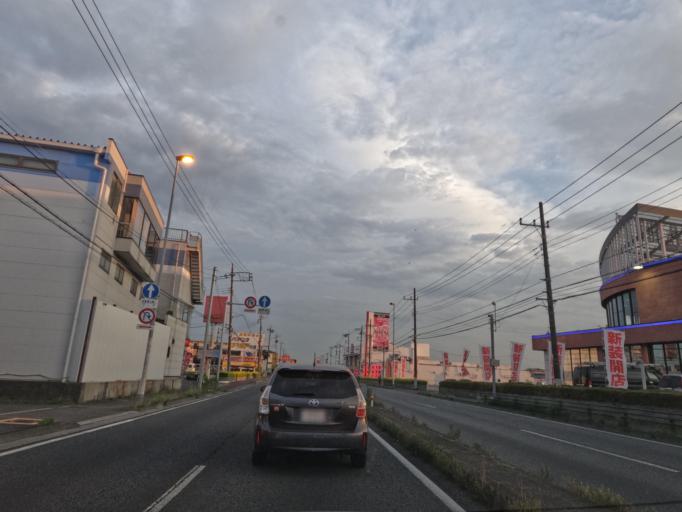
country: JP
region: Saitama
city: Koshigaya
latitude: 35.9105
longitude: 139.7695
